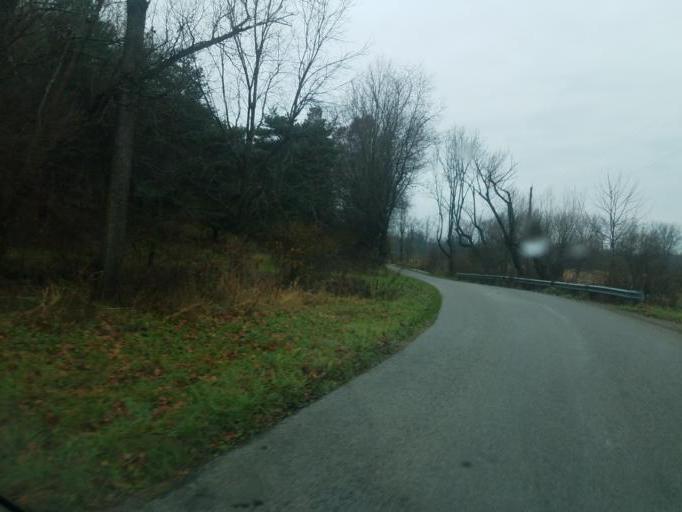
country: US
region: Ohio
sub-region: Sandusky County
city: Bellville
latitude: 40.6204
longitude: -82.5362
